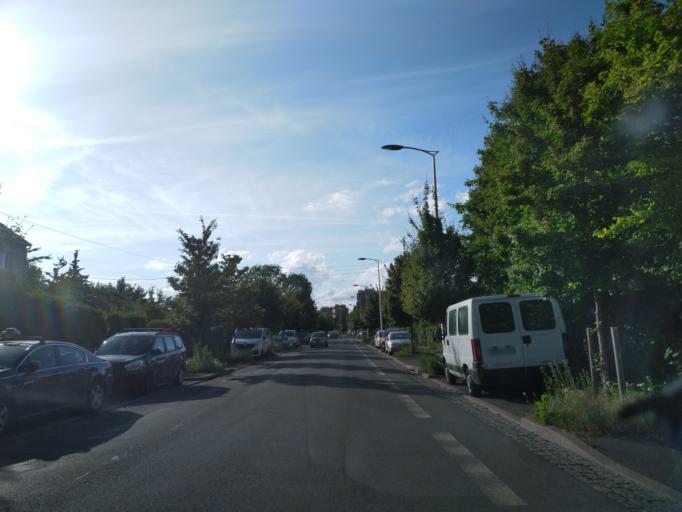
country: FR
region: Ile-de-France
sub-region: Departement de Seine-Saint-Denis
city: Noisy-le-Sec
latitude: 48.8903
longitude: 2.4696
